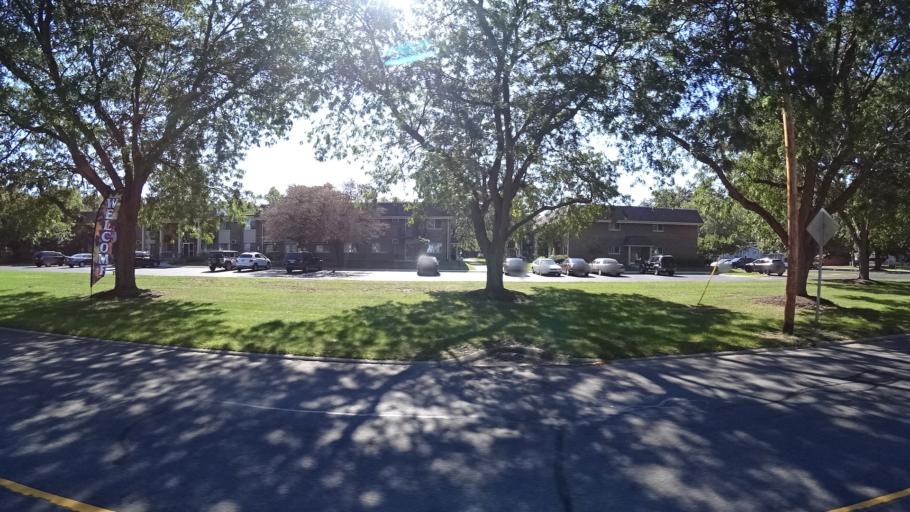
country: US
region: Indiana
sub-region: LaPorte County
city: Michigan City
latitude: 41.6876
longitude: -86.8894
